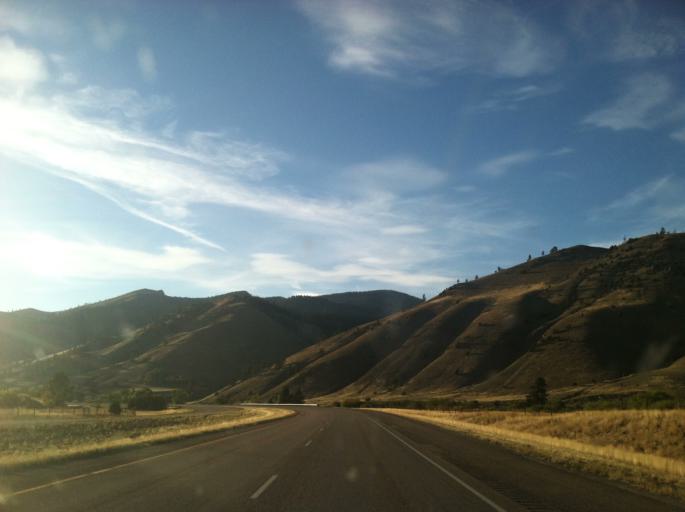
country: US
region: Montana
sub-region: Missoula County
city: Clinton
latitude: 46.7042
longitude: -113.3694
